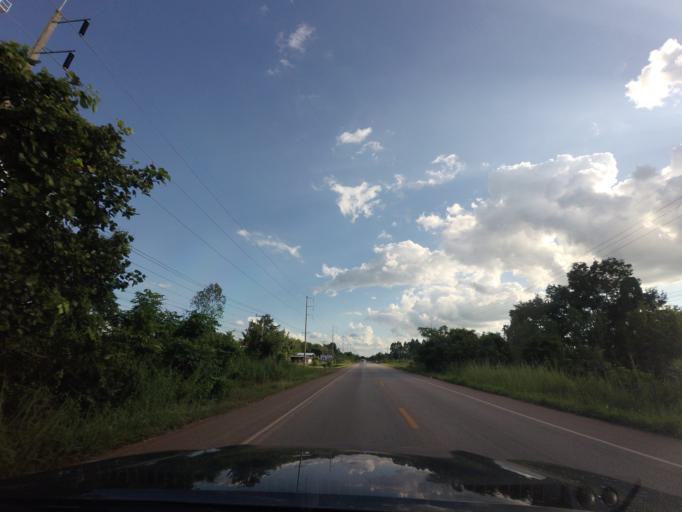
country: TH
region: Changwat Udon Thani
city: Thung Fon
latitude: 17.4813
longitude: 103.1956
